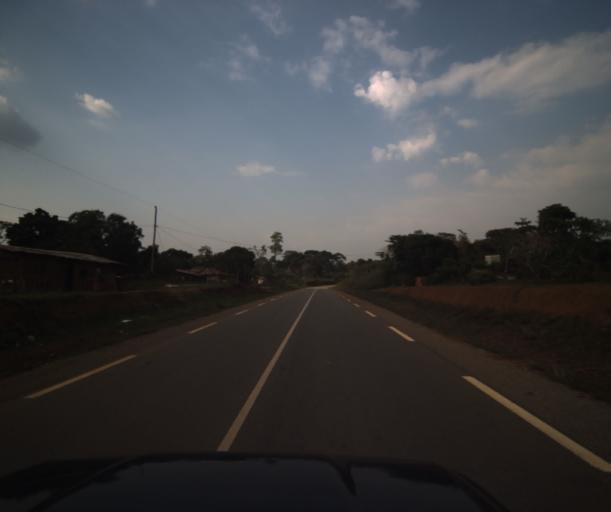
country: CM
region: Centre
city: Mbankomo
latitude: 3.6481
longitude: 11.3318
